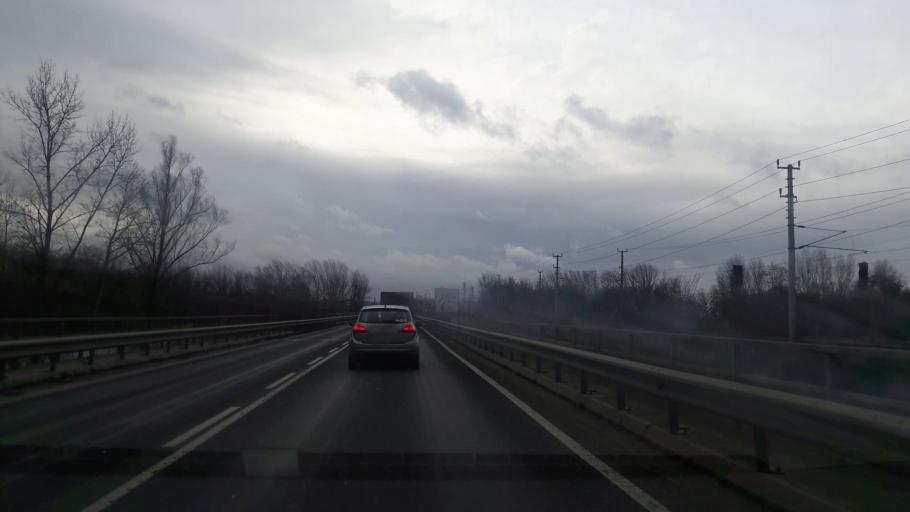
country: AT
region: Lower Austria
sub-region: Politischer Bezirk Tulln
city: Tulln
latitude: 48.3434
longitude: 16.0593
